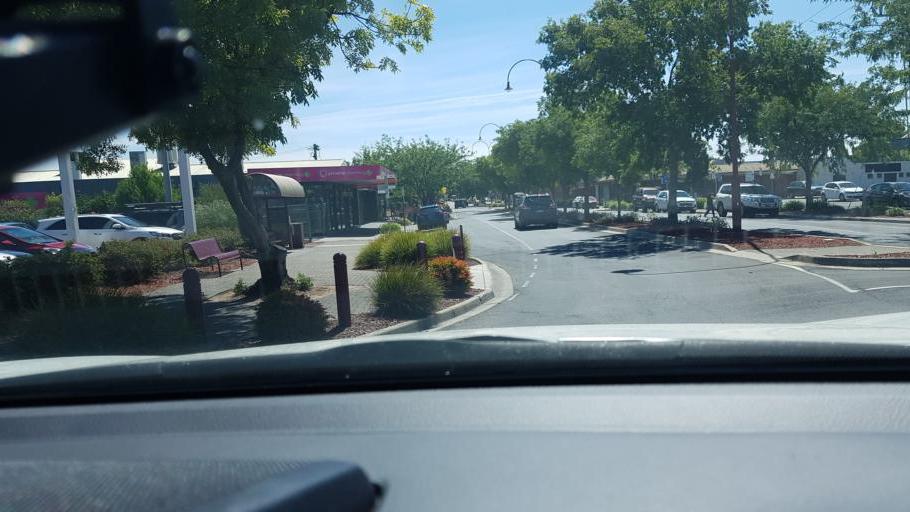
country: AU
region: Victoria
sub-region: Horsham
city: Horsham
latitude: -36.7155
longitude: 142.1971
